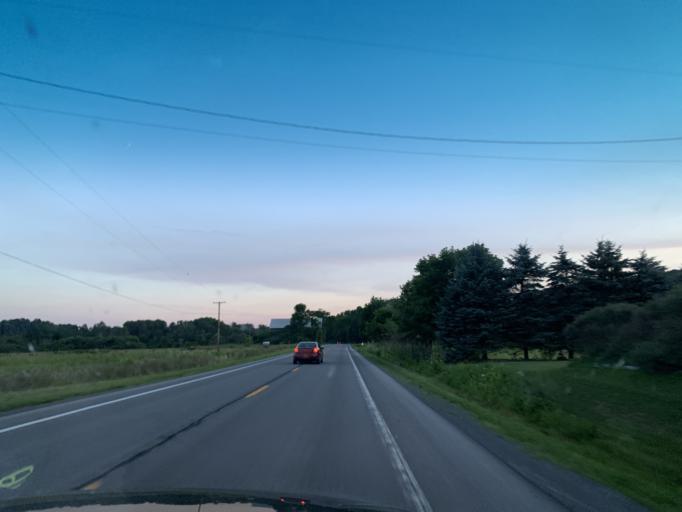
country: US
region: New York
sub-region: Chenango County
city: New Berlin
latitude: 42.7568
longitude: -75.2873
